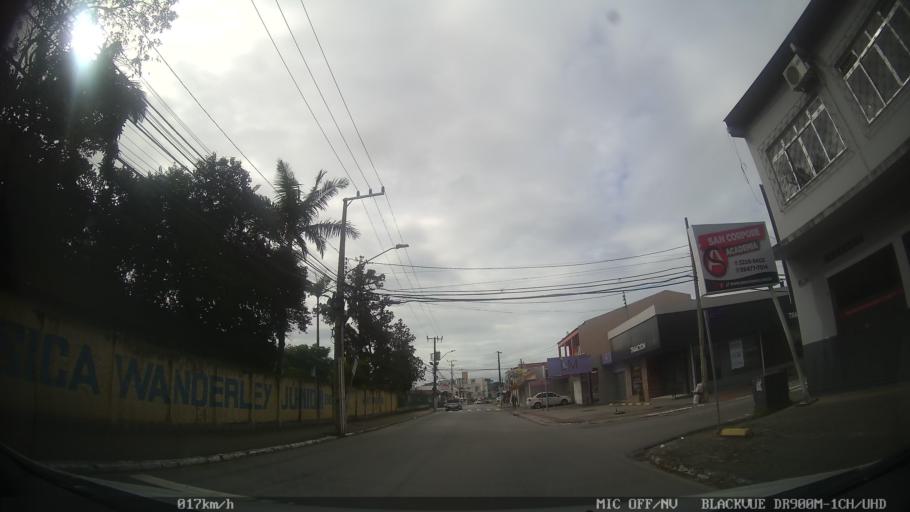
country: BR
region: Santa Catarina
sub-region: Sao Jose
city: Campinas
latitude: -27.5617
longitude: -48.6202
